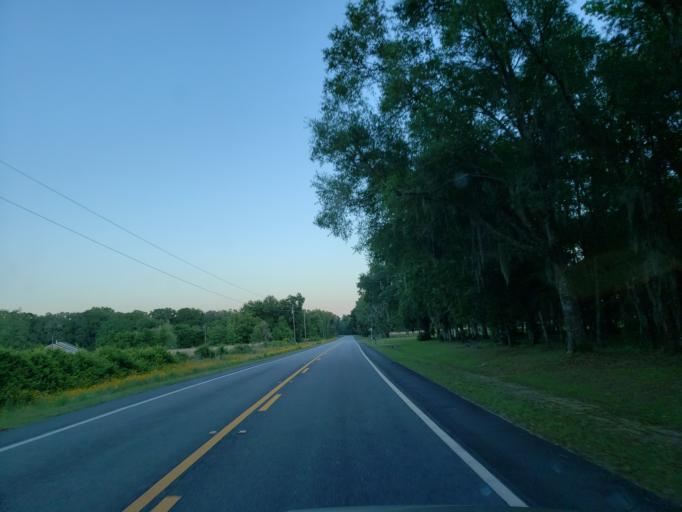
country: US
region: Georgia
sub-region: Echols County
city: Statenville
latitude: 30.5582
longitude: -83.1276
